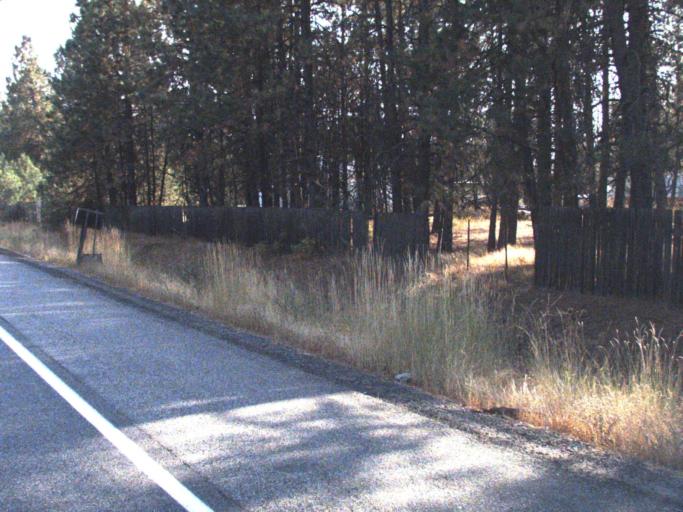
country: US
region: Washington
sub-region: Spokane County
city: Deer Park
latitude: 48.0351
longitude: -117.3498
